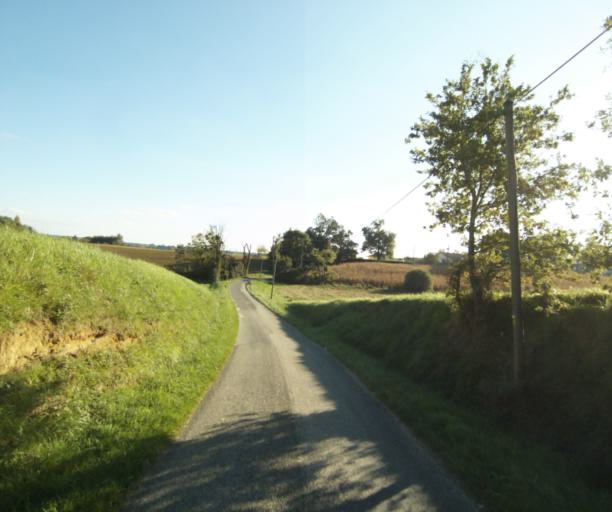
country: FR
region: Midi-Pyrenees
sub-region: Departement du Gers
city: Eauze
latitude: 43.7651
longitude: 0.1578
